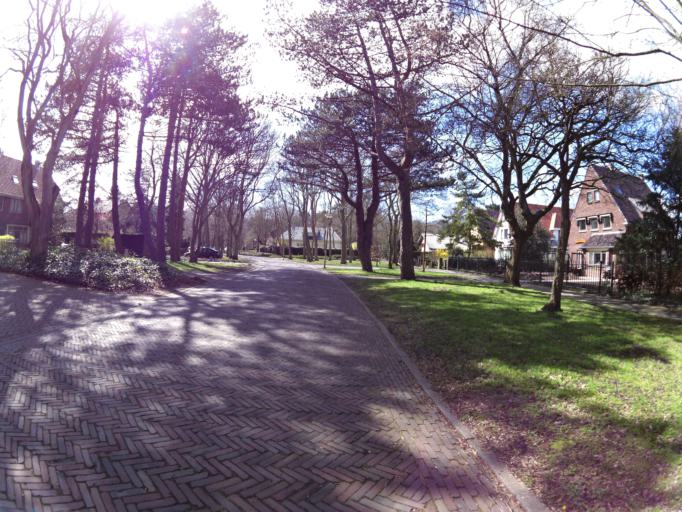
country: NL
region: South Holland
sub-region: Gemeente Hellevoetsluis
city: Nieuw-Helvoet
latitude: 51.8740
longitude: 4.0583
